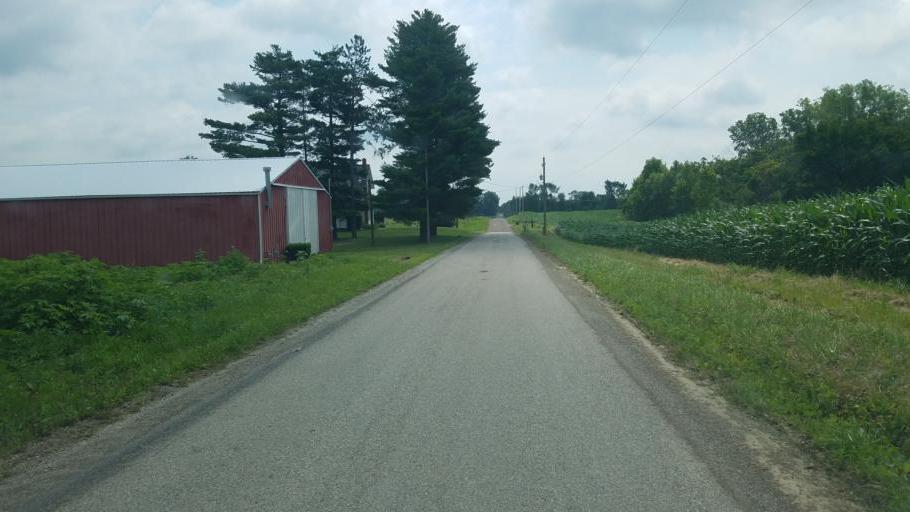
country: US
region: Ohio
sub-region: Licking County
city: Utica
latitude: 40.2912
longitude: -82.5668
